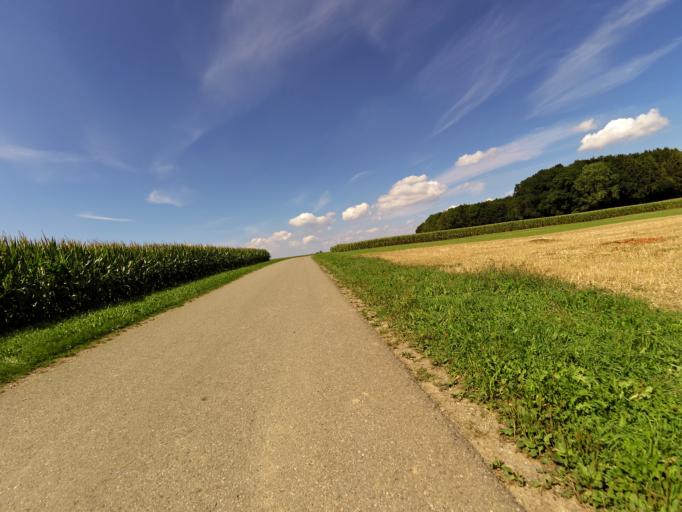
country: CH
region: Thurgau
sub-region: Weinfelden District
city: Maerstetten-Dorf
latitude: 47.6241
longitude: 9.0786
